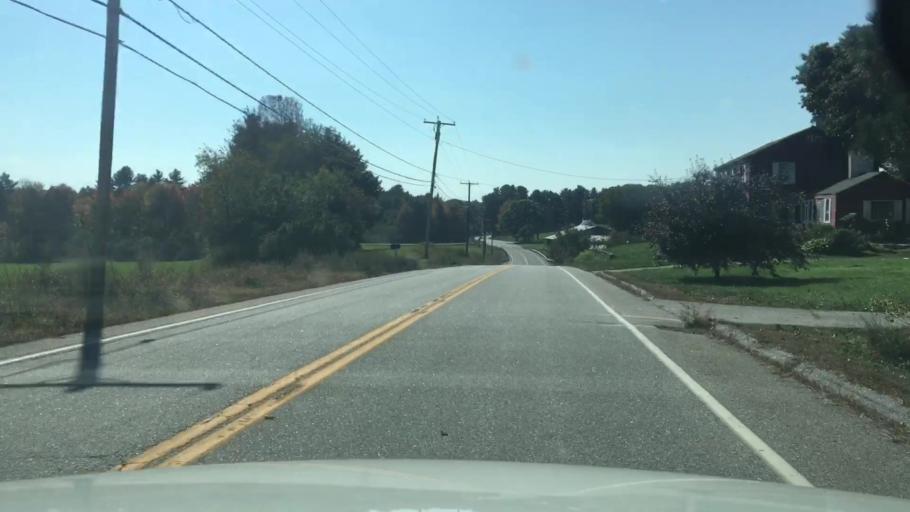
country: US
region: Maine
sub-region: Androscoggin County
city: Lisbon Falls
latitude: 44.0254
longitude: -70.0396
